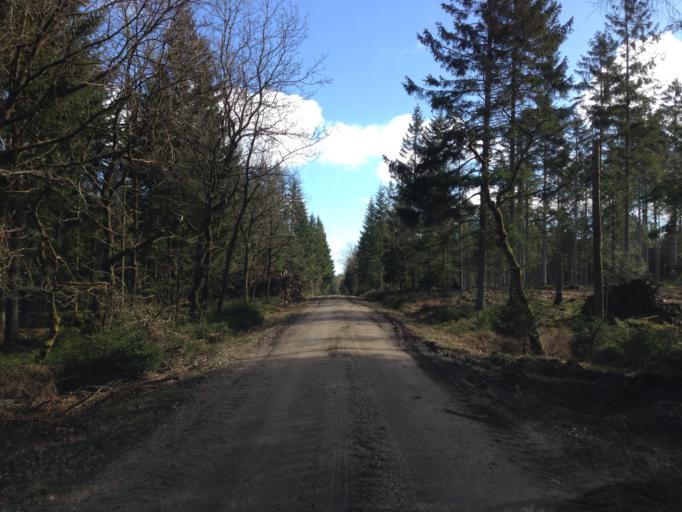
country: DK
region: Central Jutland
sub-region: Holstebro Kommune
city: Ulfborg
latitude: 56.2741
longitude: 8.4566
